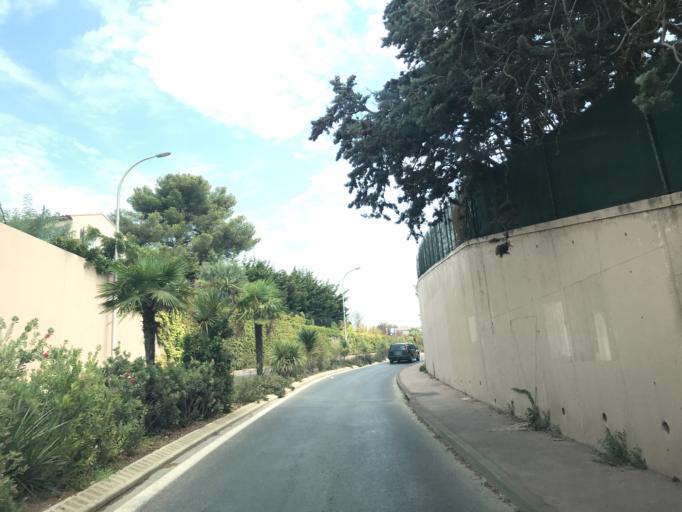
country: FR
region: Provence-Alpes-Cote d'Azur
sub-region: Departement du Var
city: Six-Fours-les-Plages
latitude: 43.0858
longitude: 5.8240
